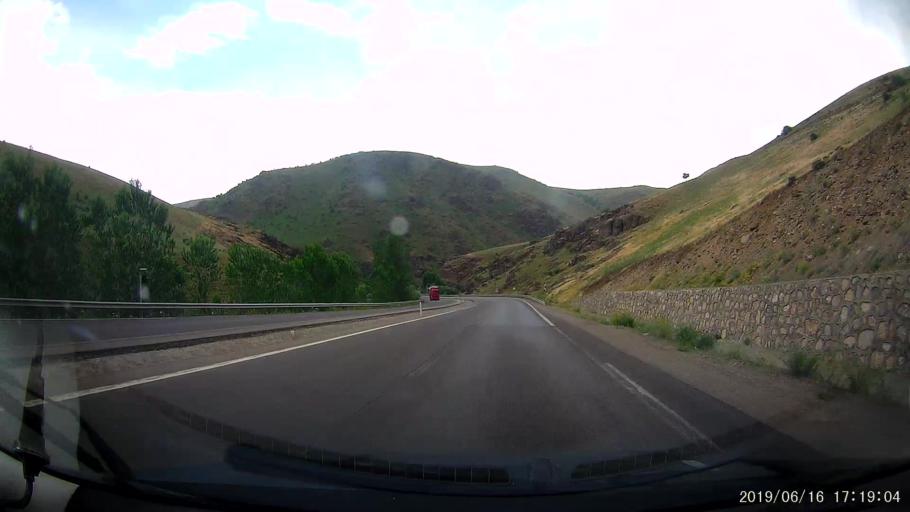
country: TR
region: Erzincan
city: Tercan
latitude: 39.8051
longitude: 40.5314
